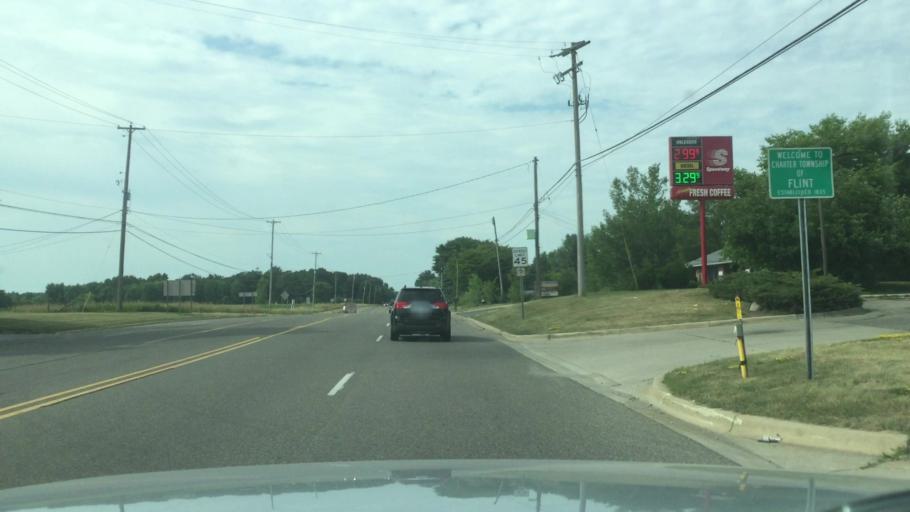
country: US
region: Michigan
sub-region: Genesee County
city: Swartz Creek
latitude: 43.0016
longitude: -83.8120
